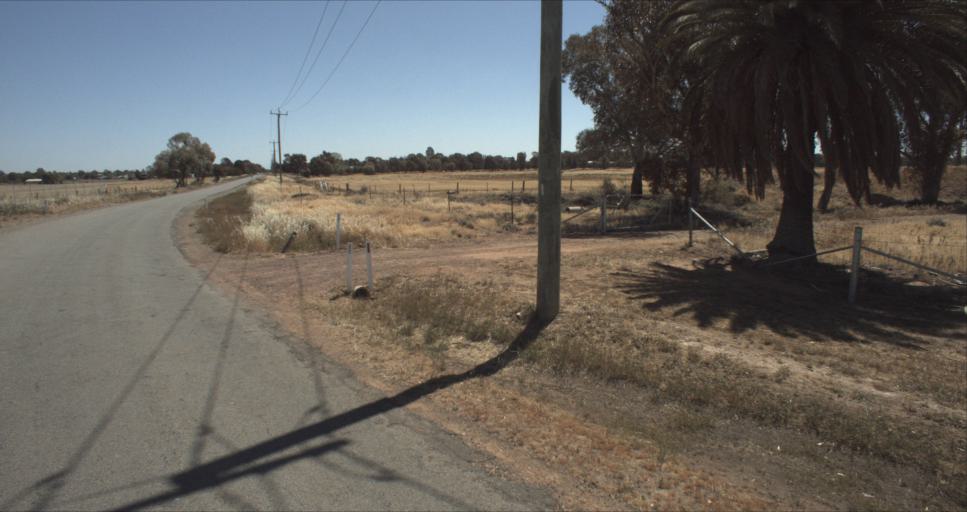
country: AU
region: New South Wales
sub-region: Leeton
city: Leeton
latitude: -34.5448
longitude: 146.4262
